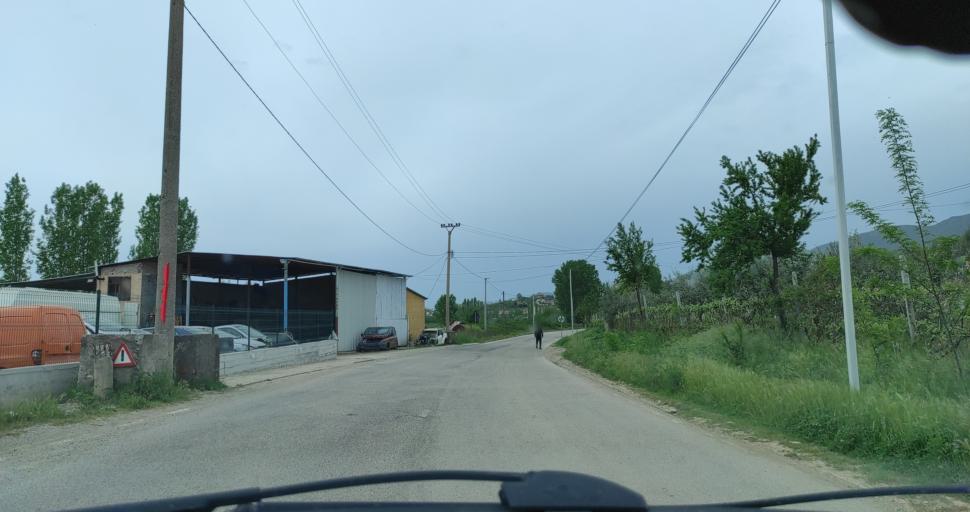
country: AL
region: Lezhe
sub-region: Rrethi i Kurbinit
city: Lac
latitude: 41.6126
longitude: 19.7113
